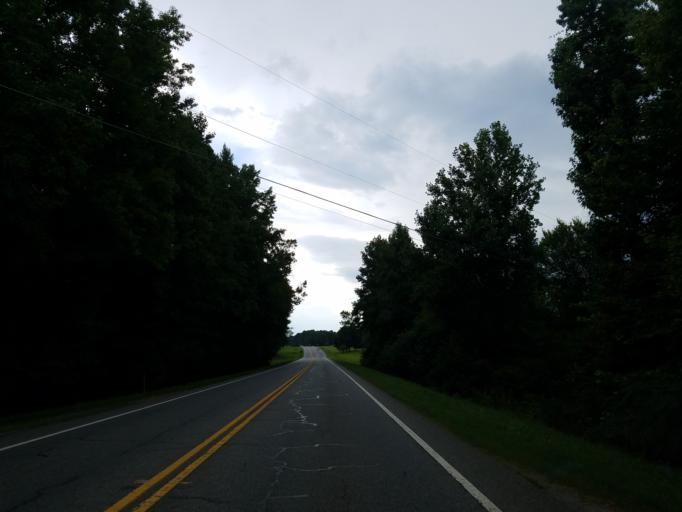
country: US
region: Georgia
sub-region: Bartow County
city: Adairsville
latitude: 34.3397
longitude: -84.9069
